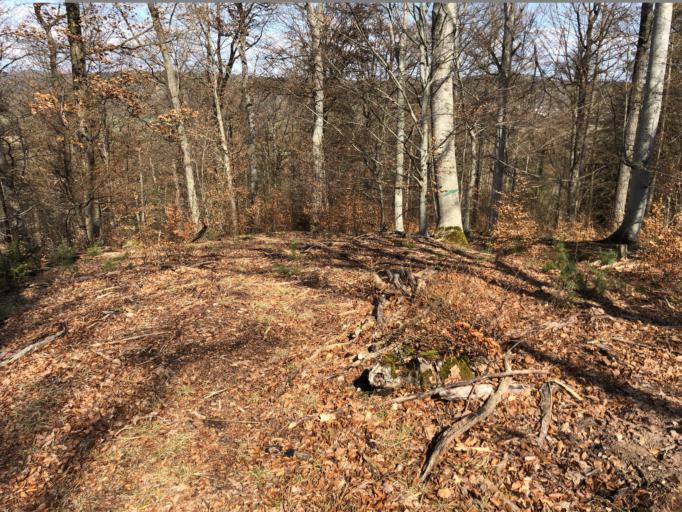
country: DE
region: Baden-Wuerttemberg
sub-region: Tuebingen Region
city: Tuebingen
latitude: 48.5139
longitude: 9.0091
